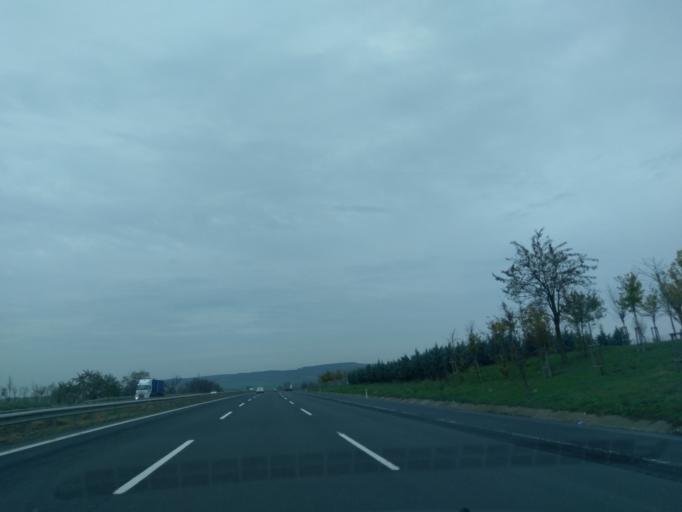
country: TR
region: Istanbul
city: Canta
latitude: 41.1441
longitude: 28.1478
